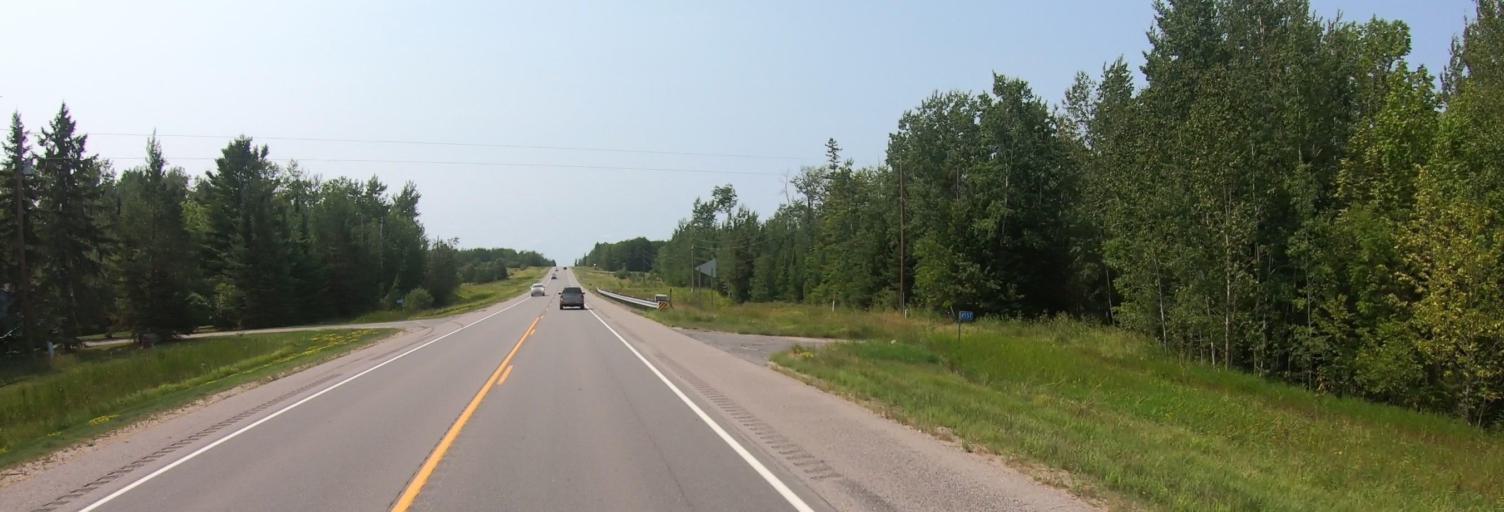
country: US
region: Minnesota
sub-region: Koochiching County
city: International Falls
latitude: 48.5421
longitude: -93.4669
